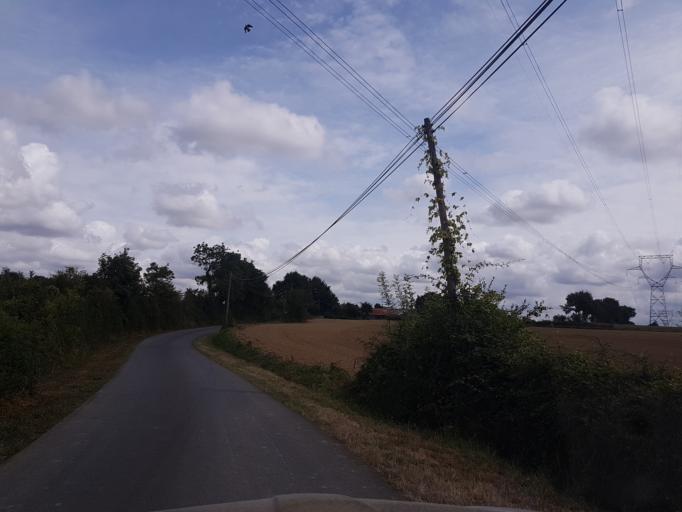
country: FR
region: Pays de la Loire
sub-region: Departement de la Loire-Atlantique
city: Les Touches
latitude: 47.4231
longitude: -1.4477
